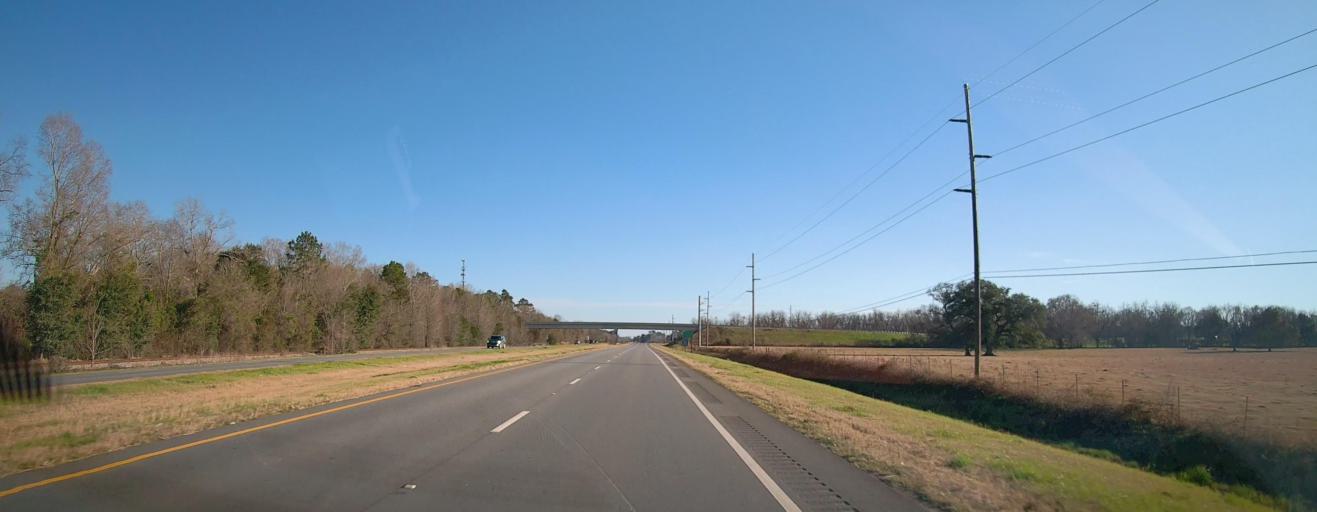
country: US
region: Georgia
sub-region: Lee County
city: Leesburg
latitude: 31.7502
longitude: -84.1809
